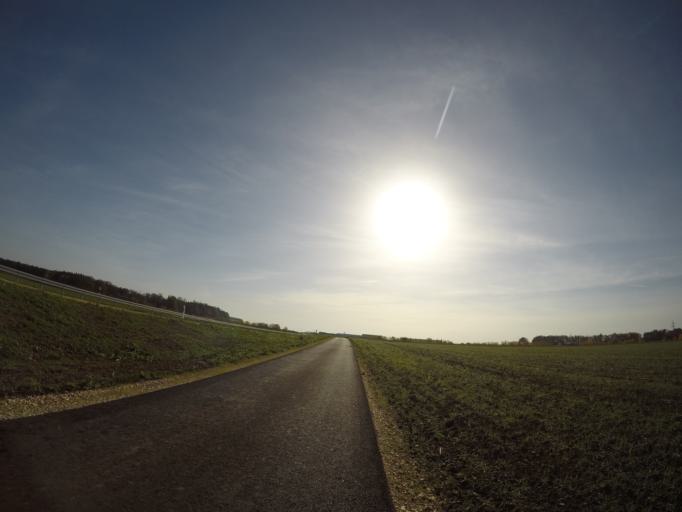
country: DE
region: Baden-Wuerttemberg
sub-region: Tuebingen Region
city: Beimerstetten
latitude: 48.4719
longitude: 9.9675
